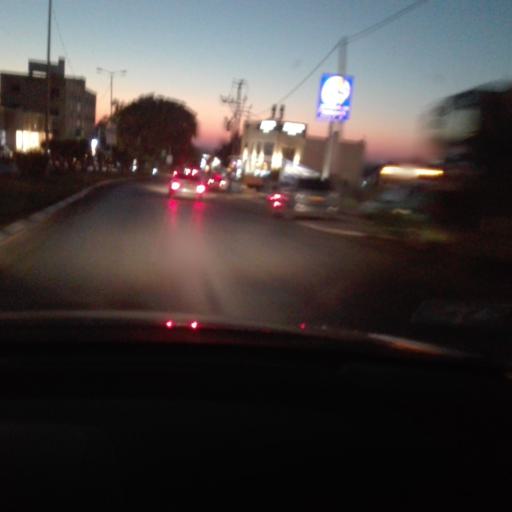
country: PS
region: West Bank
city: Nazlat `Isa
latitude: 32.4243
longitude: 35.0369
